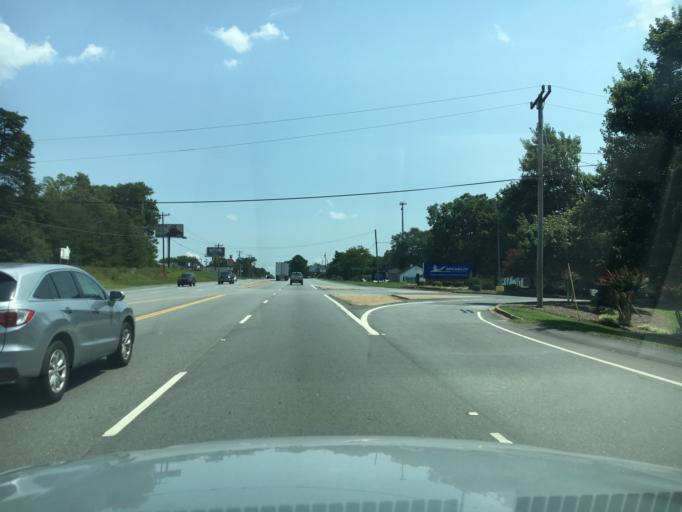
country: US
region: South Carolina
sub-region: Anderson County
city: Pendleton
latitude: 34.6023
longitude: -82.7582
